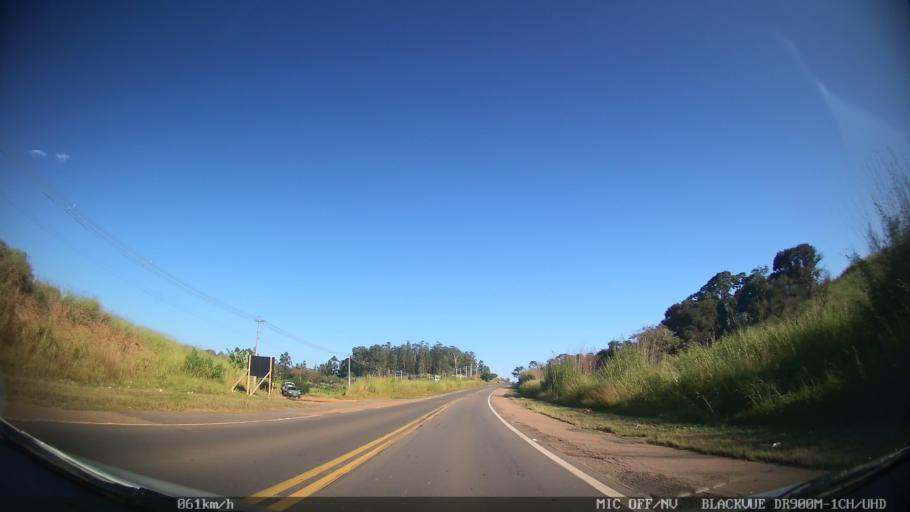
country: BR
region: Sao Paulo
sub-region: Vinhedo
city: Vinhedo
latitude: -23.0541
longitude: -47.0608
